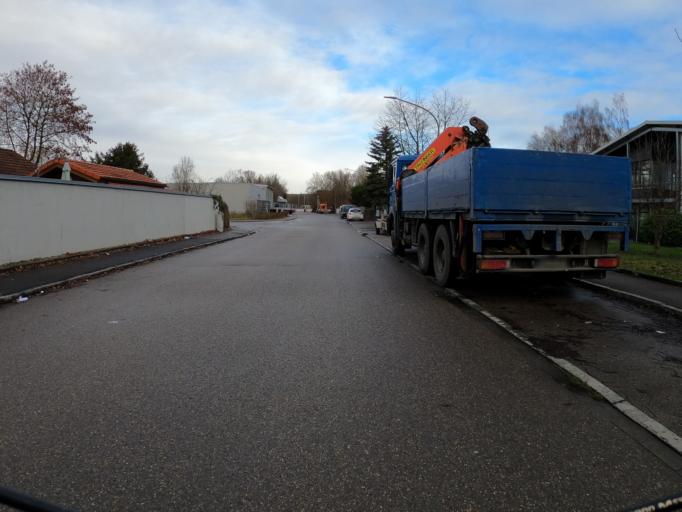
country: DE
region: Bavaria
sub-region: Swabia
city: Holzheim
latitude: 48.4241
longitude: 10.0672
